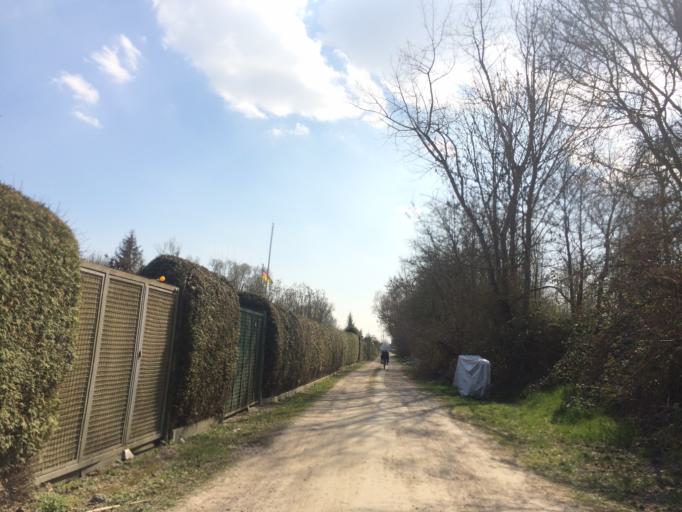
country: DE
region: Bavaria
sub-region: Swabia
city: Gersthofen
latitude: 48.4049
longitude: 10.8873
